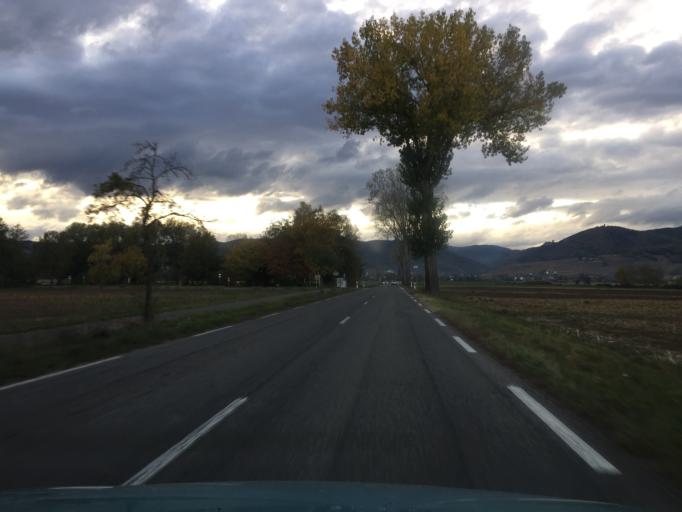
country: FR
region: Alsace
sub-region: Departement du Haut-Rhin
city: Bergheim
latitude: 48.1888
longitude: 7.3618
